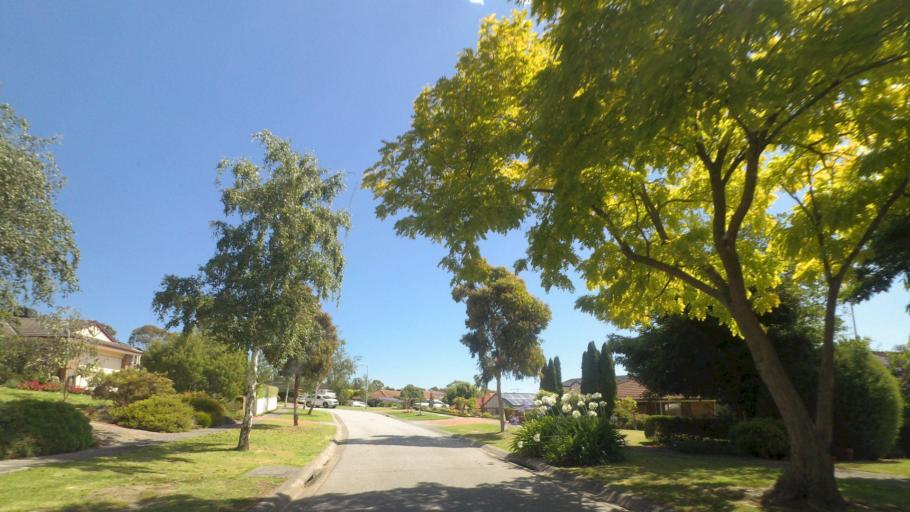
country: AU
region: Victoria
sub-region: Yarra Ranges
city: Kilsyth
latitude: -37.8051
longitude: 145.3322
